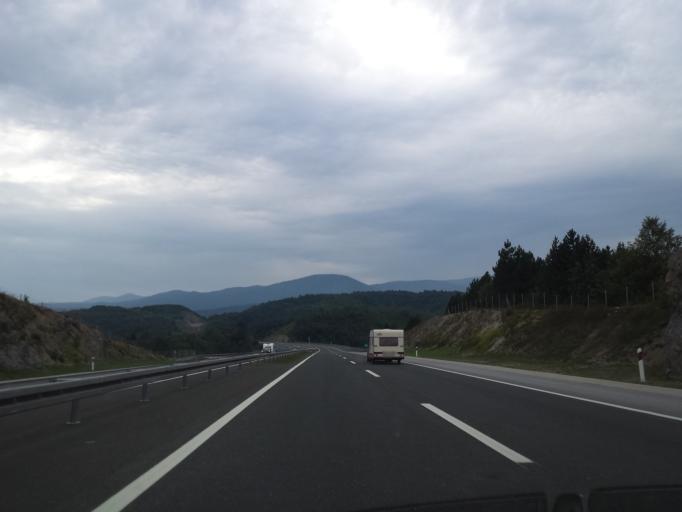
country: HR
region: Karlovacka
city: Ostarije
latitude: 45.1589
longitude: 15.2728
